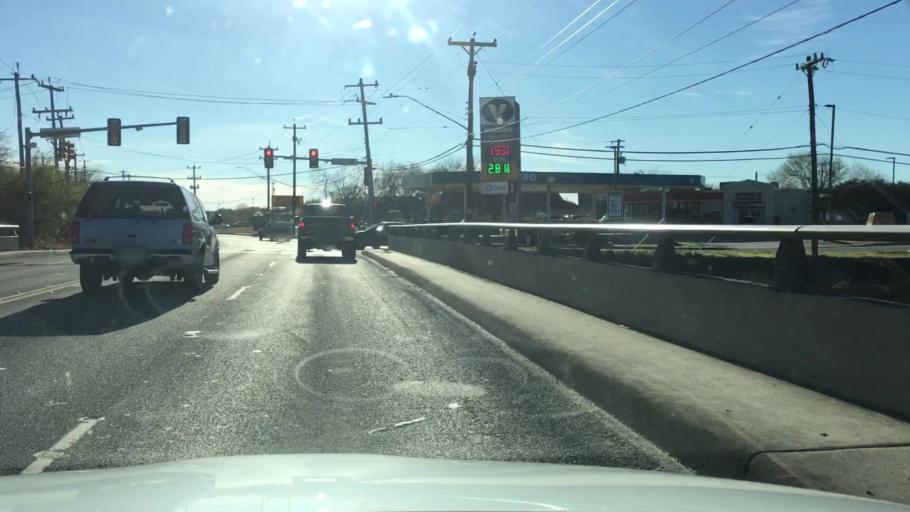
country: US
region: Texas
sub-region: Bexar County
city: Windcrest
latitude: 29.5346
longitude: -98.4284
